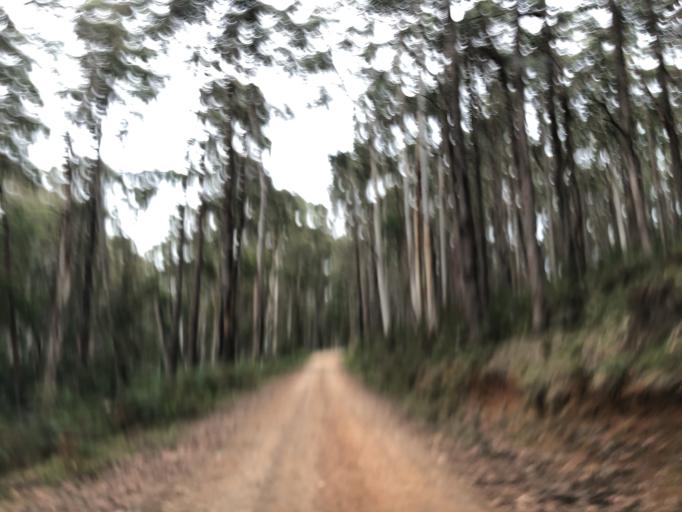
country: AU
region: Victoria
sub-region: Moorabool
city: Bacchus Marsh
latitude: -37.4534
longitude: 144.2502
